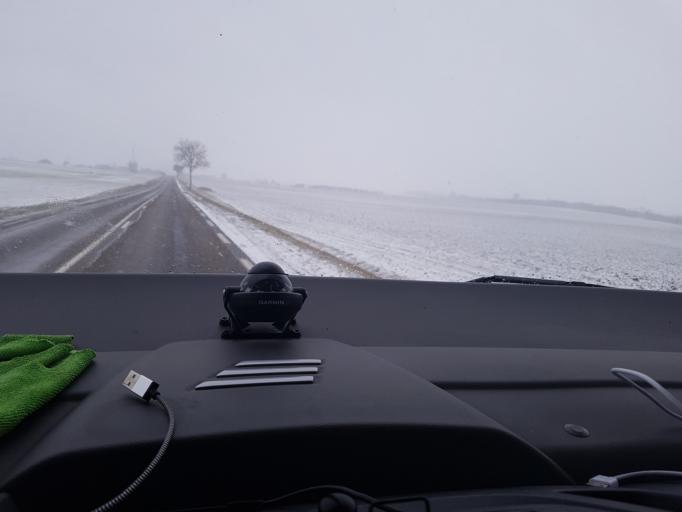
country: FR
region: Lorraine
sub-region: Departement de la Moselle
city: Solgne
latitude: 48.8974
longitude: 6.3577
